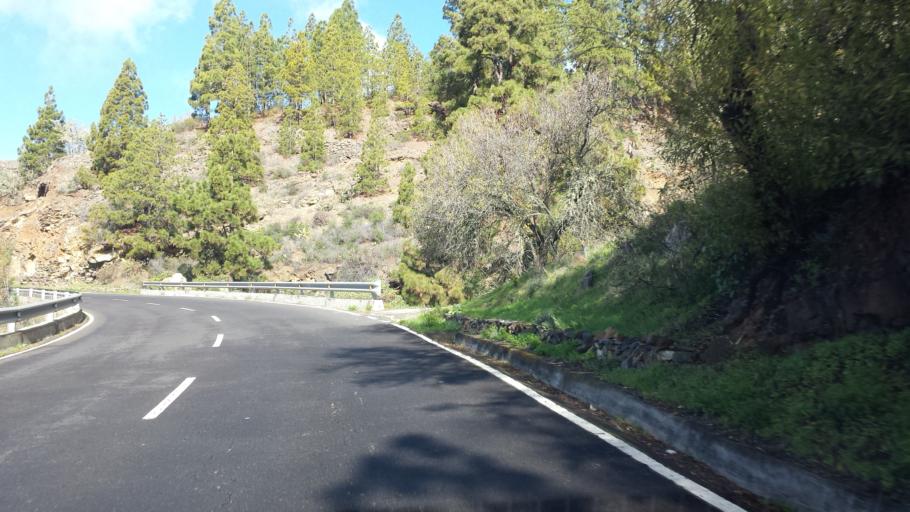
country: ES
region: Canary Islands
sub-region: Provincia de Santa Cruz de Tenerife
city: Puntagorda
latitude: 28.7340
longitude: -17.9653
